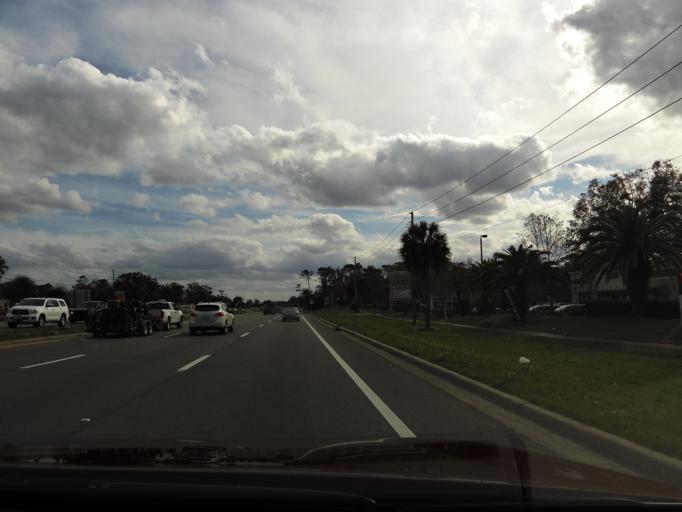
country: US
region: Florida
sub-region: Volusia County
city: De Land Southwest
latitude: 28.9978
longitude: -81.3027
